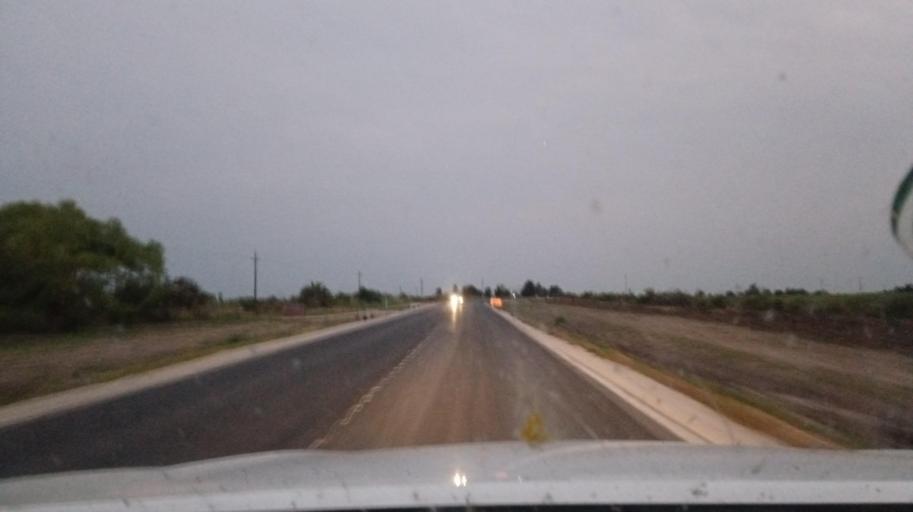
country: UY
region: Canelones
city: Sauce
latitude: -34.5721
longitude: -56.1009
